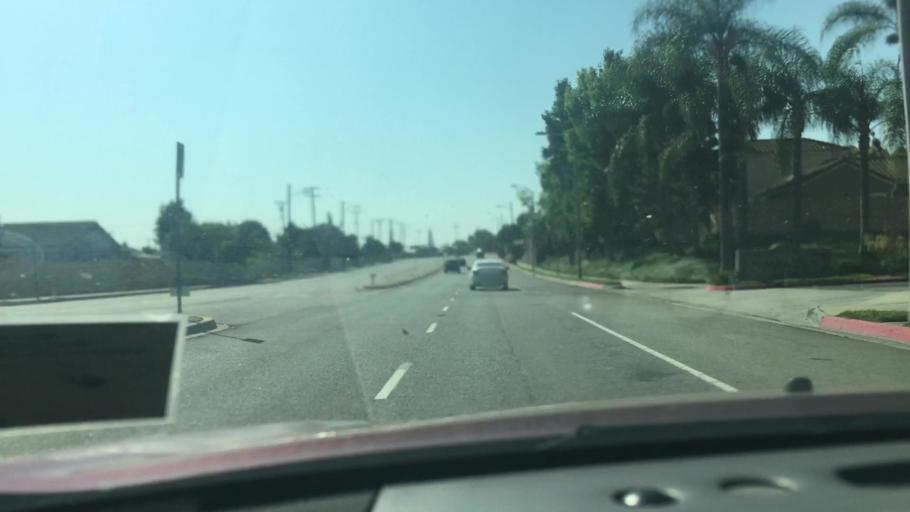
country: US
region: California
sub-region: Los Angeles County
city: La Mirada
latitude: 33.9372
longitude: -118.0201
